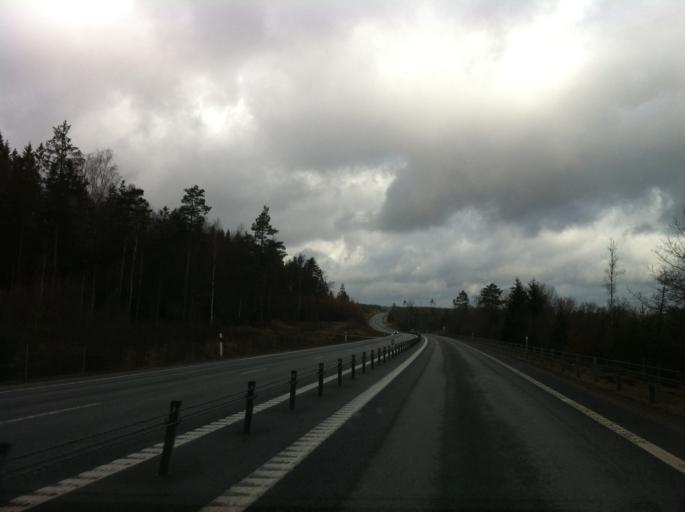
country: SE
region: Halland
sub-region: Halmstads Kommun
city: Oskarstrom
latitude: 56.8415
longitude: 13.0027
